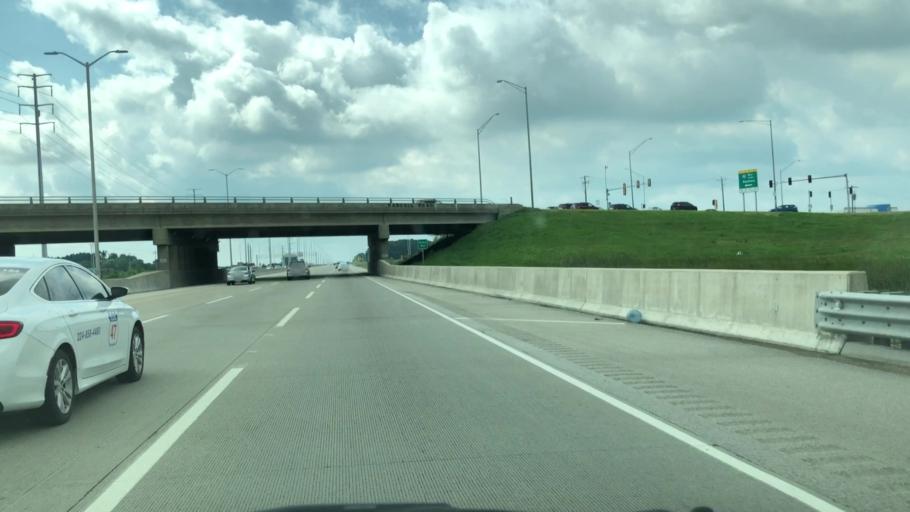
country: US
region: Illinois
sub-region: Kane County
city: Sleepy Hollow
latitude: 42.0804
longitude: -88.3345
